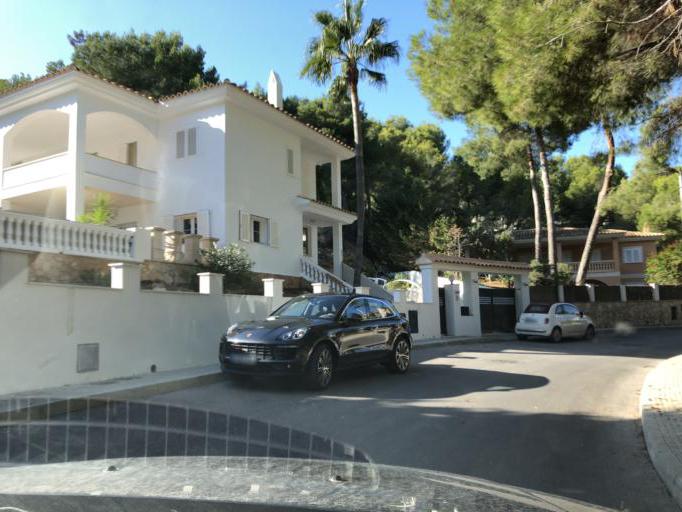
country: ES
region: Balearic Islands
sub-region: Illes Balears
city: Camp de Mar
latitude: 39.5406
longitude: 2.4083
